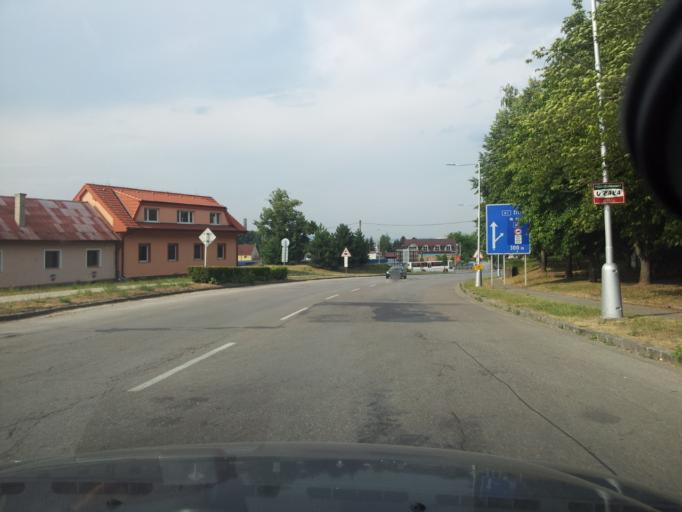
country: SK
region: Trenciansky
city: Nova Dubnica
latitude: 48.9324
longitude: 18.1176
